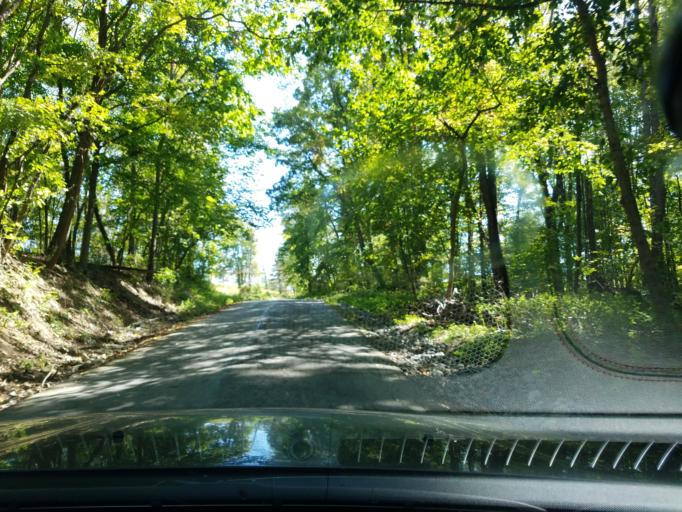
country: US
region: Pennsylvania
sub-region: Lawrence County
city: Ellwood City
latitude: 40.9330
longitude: -80.3117
